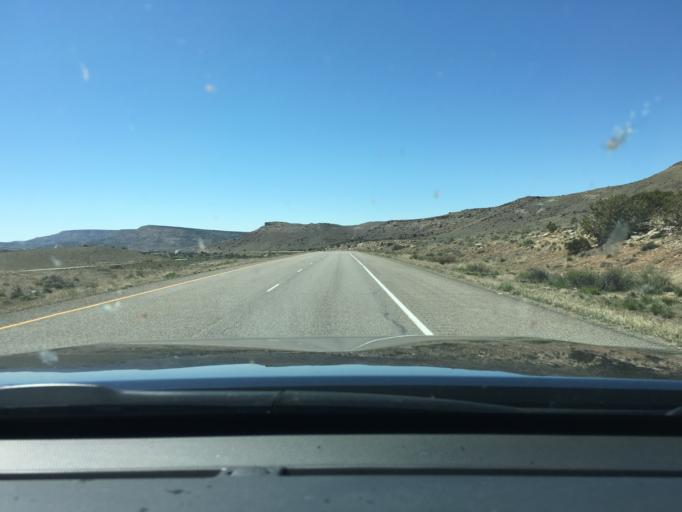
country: US
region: Colorado
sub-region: Mesa County
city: Loma
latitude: 39.2100
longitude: -108.9740
